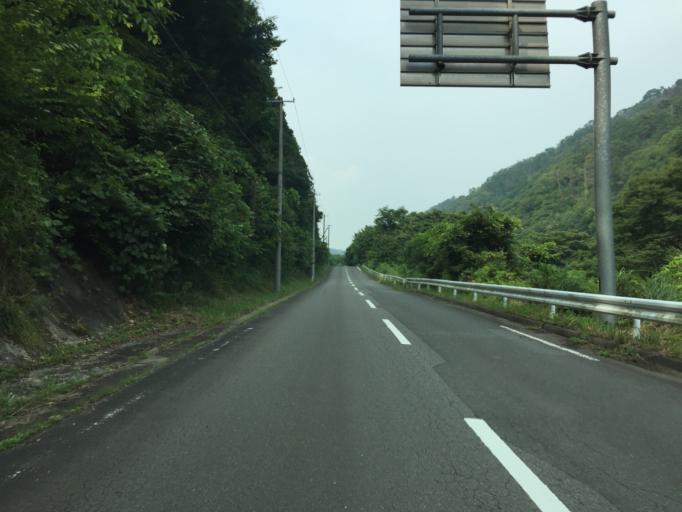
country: JP
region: Fukushima
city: Namie
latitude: 37.5797
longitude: 140.8847
